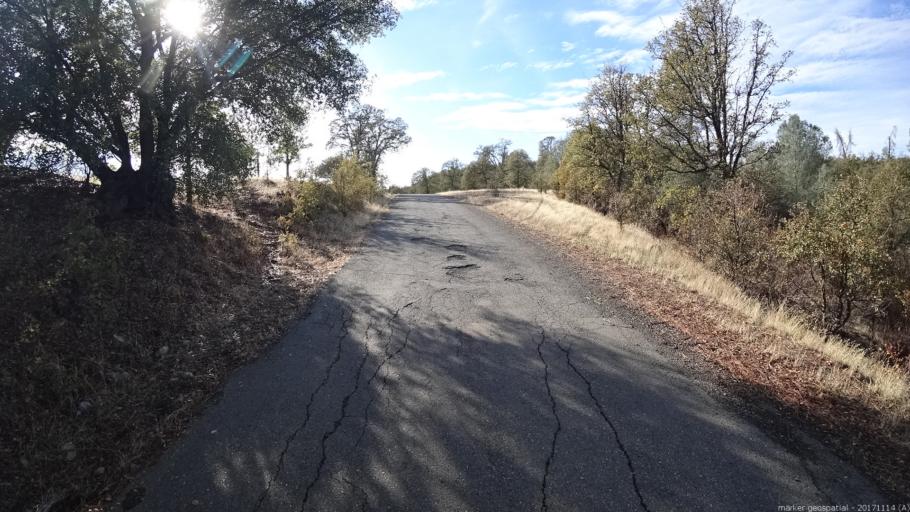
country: US
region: California
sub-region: Shasta County
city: Shasta
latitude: 40.3757
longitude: -122.5569
